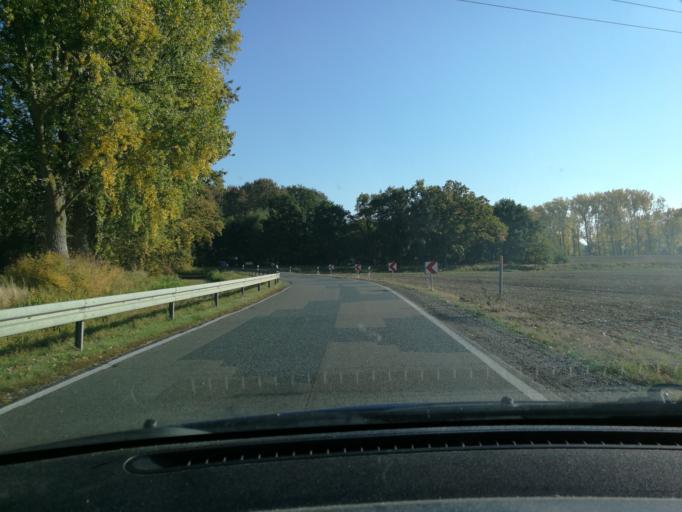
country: DE
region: Mecklenburg-Vorpommern
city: Domitz
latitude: 53.1476
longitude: 11.2597
